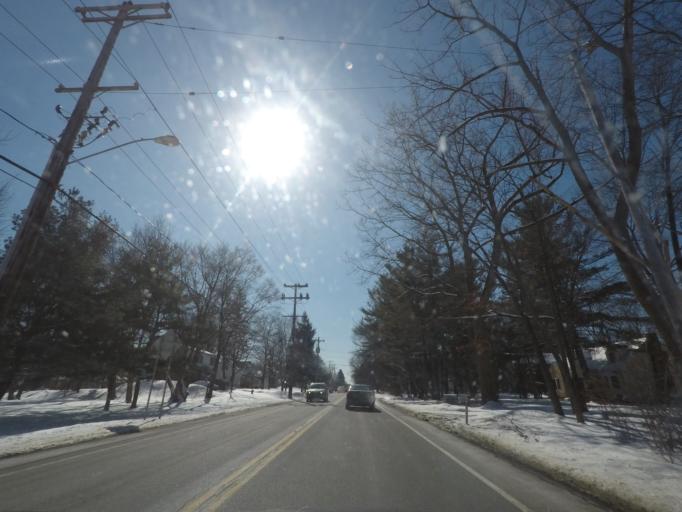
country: US
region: New York
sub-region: Schenectady County
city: Schenectady
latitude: 42.8261
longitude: -73.8921
